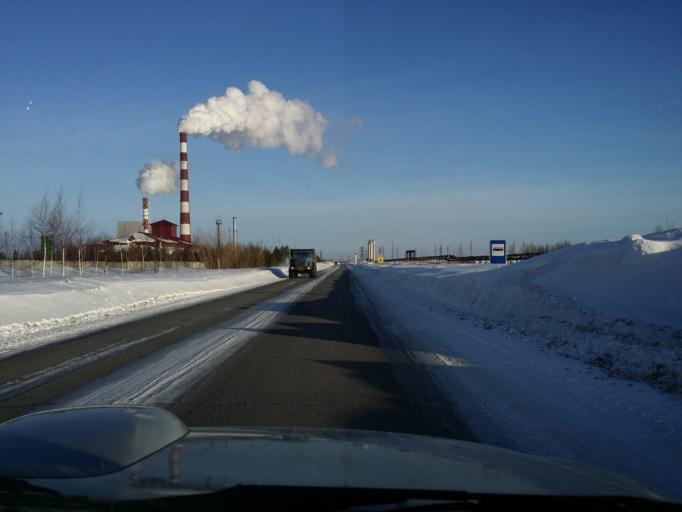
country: RU
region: Khanty-Mansiyskiy Avtonomnyy Okrug
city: Izluchinsk
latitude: 60.9792
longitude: 76.9190
